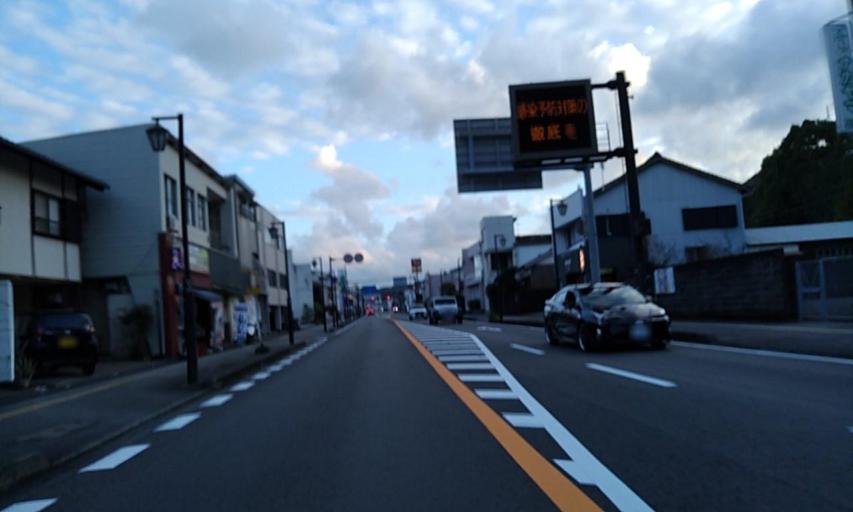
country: JP
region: Wakayama
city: Shingu
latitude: 33.7215
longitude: 135.9866
